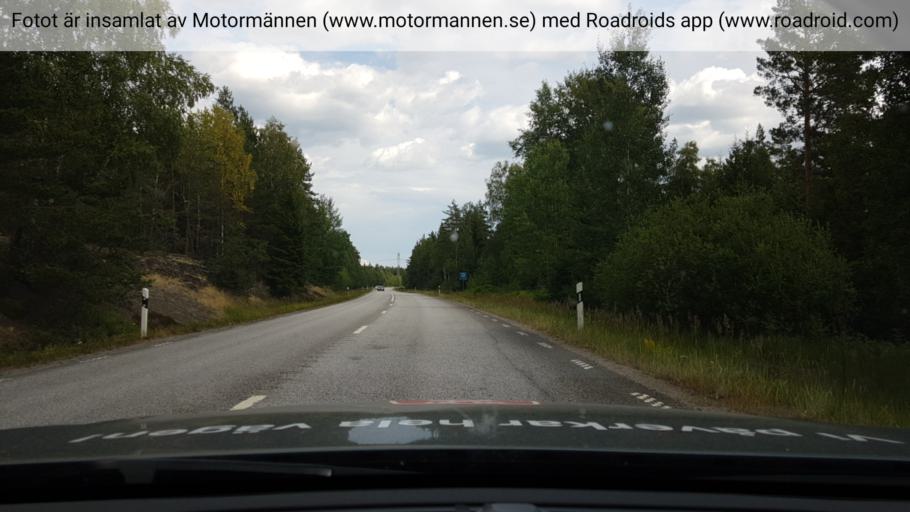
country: SE
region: Uppsala
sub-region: Enkopings Kommun
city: Orsundsbro
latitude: 59.8895
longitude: 17.1755
